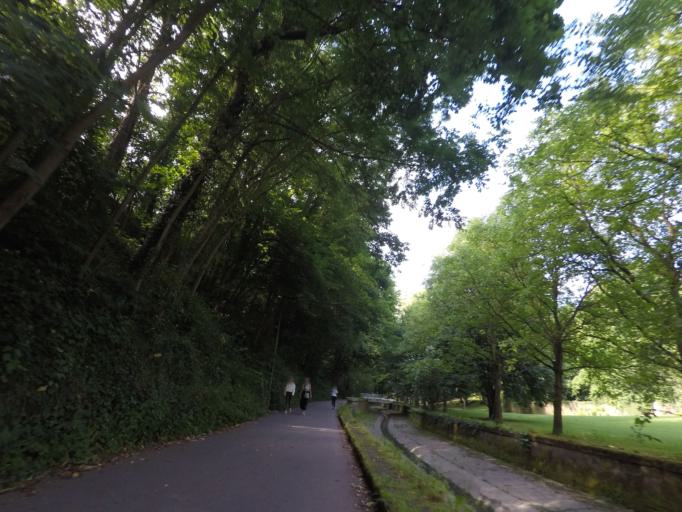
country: LU
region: Luxembourg
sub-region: Canton de Luxembourg
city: Luxembourg
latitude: 49.6058
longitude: 6.1241
